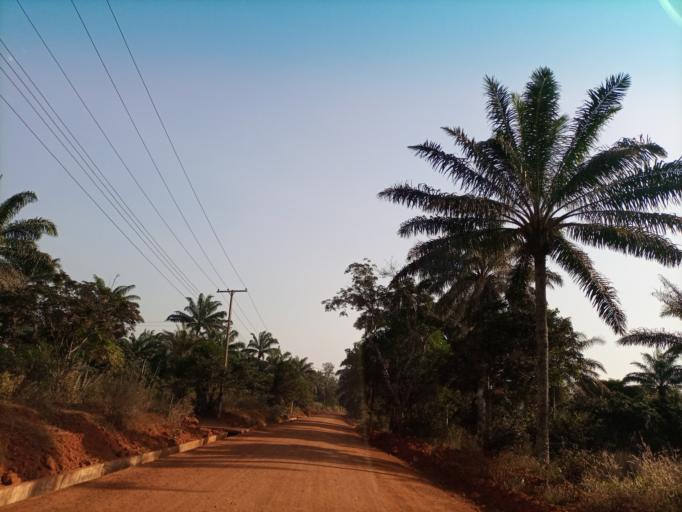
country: NG
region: Enugu
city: Opi
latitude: 6.7772
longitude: 7.3897
